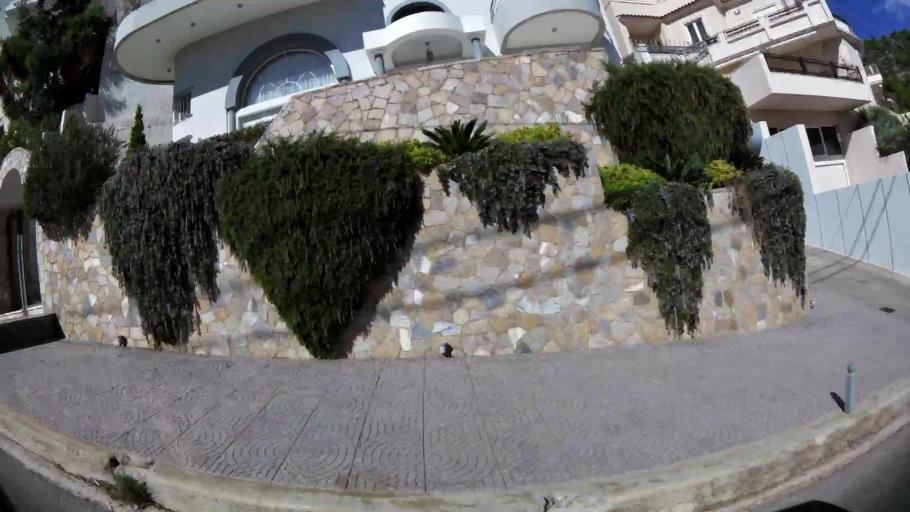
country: GR
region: Attica
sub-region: Nomarchia Anatolikis Attikis
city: Voula
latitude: 37.8561
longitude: 23.7844
